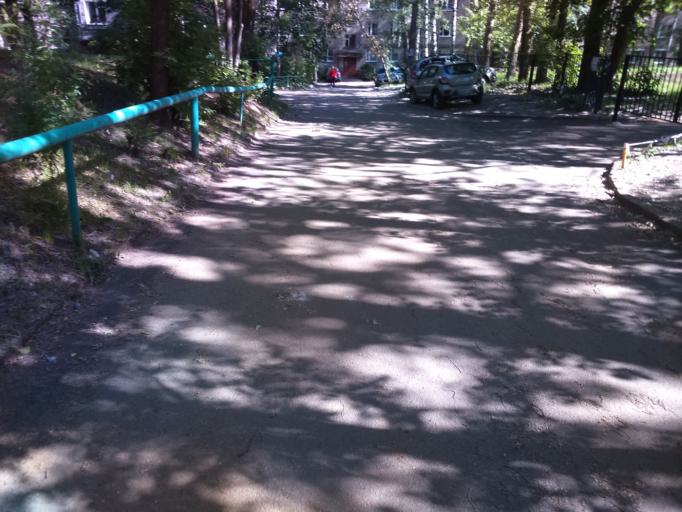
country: RU
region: Jaroslavl
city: Yaroslavl
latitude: 57.5773
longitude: 39.8520
